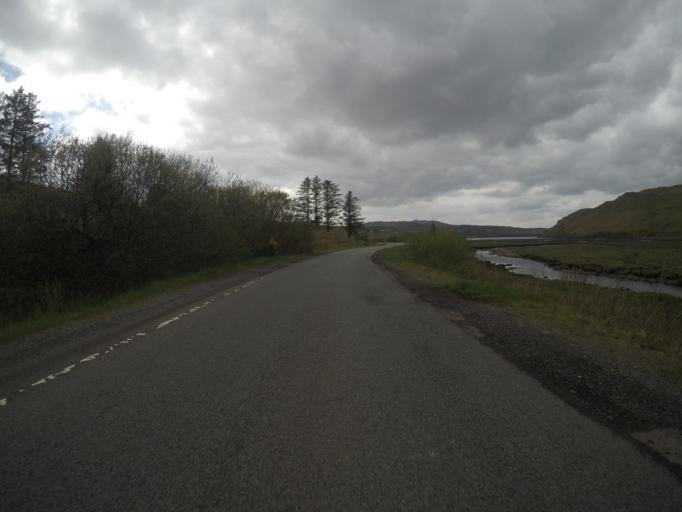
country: GB
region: Scotland
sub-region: Highland
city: Isle of Skye
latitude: 57.2976
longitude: -6.3102
